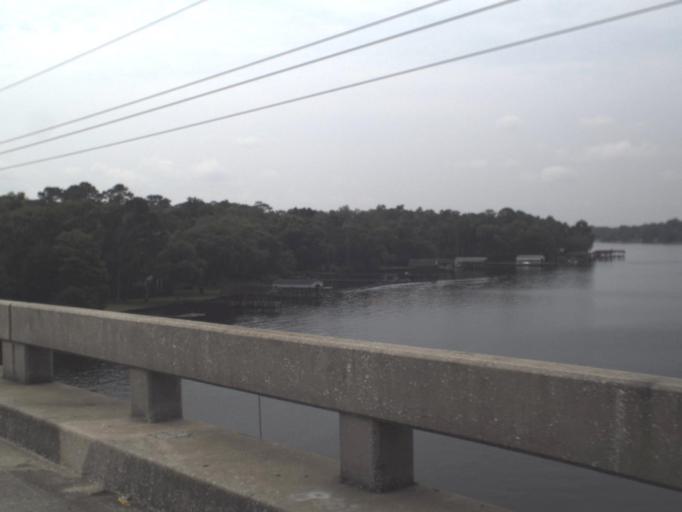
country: US
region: Florida
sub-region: Duval County
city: Jacksonville
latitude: 30.2739
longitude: -81.7169
